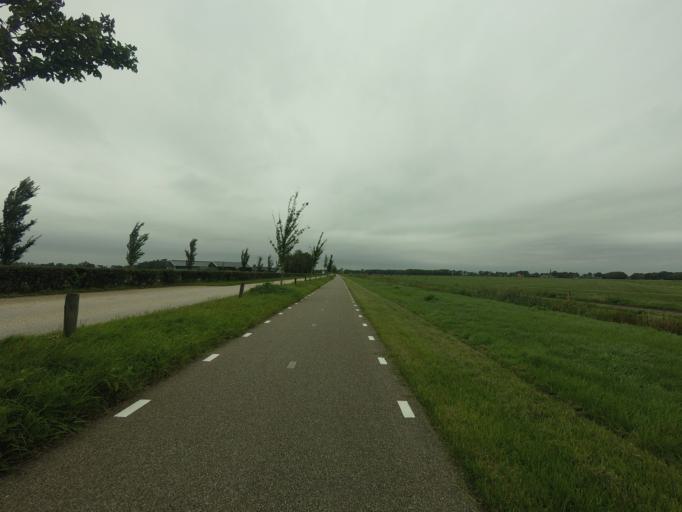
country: NL
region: Friesland
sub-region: Gemeente Opsterland
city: Gorredijk
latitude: 53.0090
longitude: 6.0379
